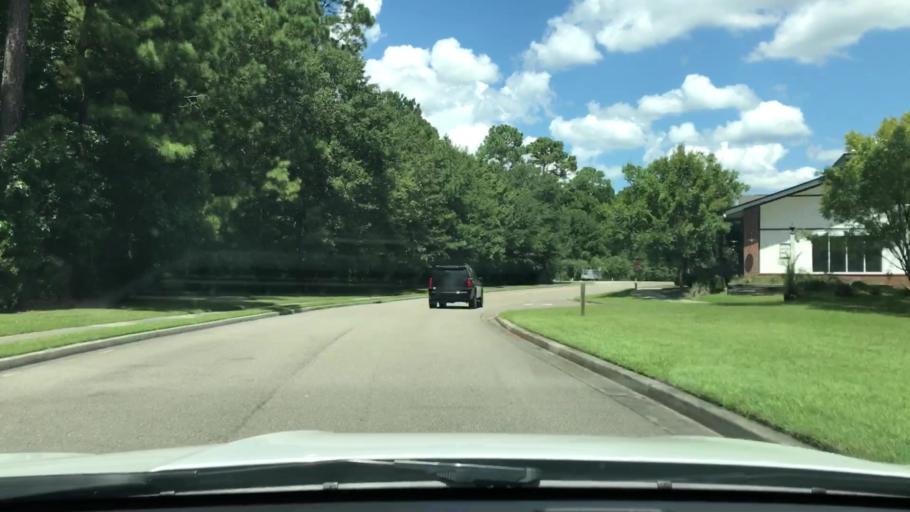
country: US
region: South Carolina
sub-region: Berkeley County
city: Hanahan
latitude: 32.9320
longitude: -79.9998
